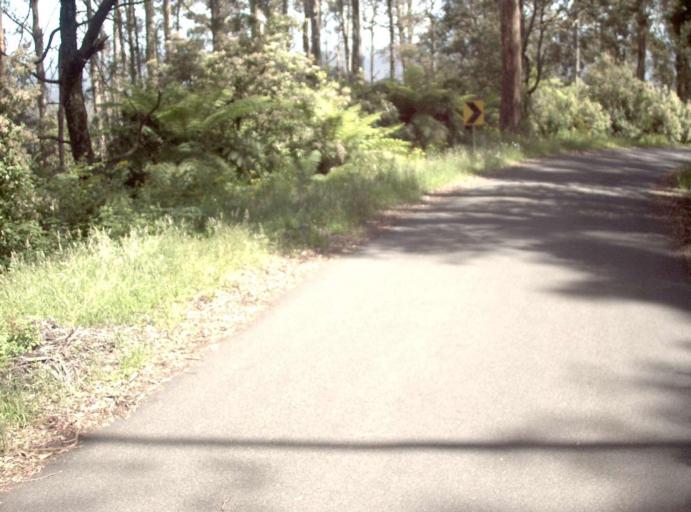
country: AU
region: Victoria
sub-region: Latrobe
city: Moe
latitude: -37.8552
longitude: 146.2374
